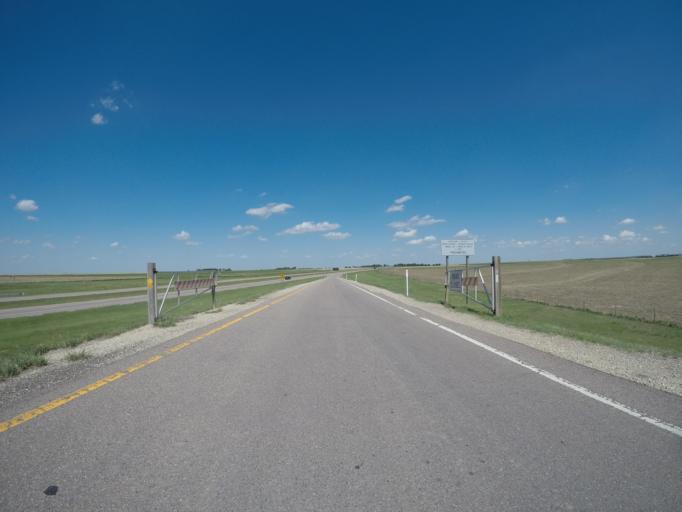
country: US
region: Kansas
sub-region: Gove County
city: Gove
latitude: 39.1019
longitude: -100.4432
